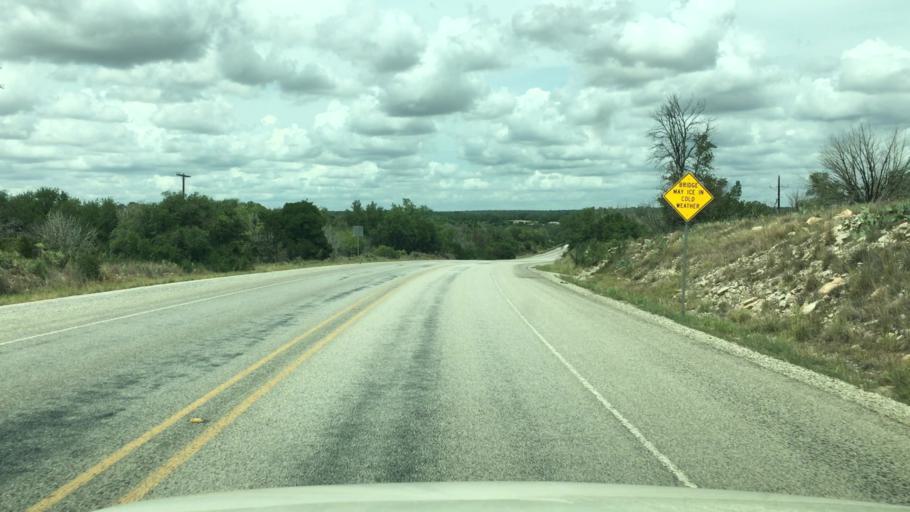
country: US
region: Texas
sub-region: McCulloch County
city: Brady
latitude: 31.0104
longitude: -99.2075
